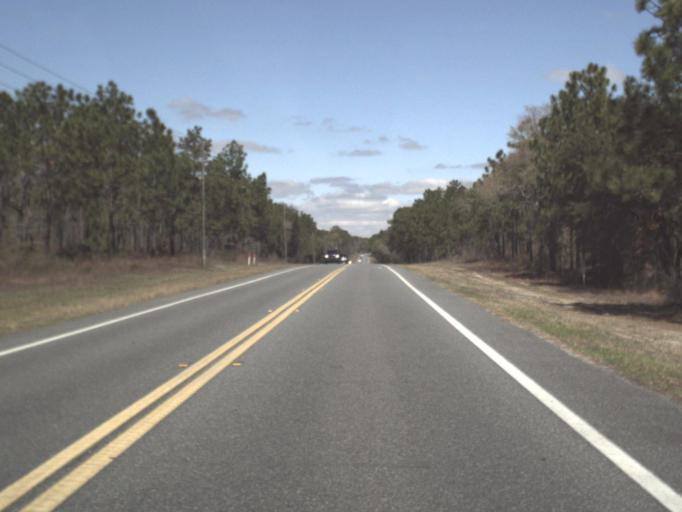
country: US
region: Florida
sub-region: Wakulla County
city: Crawfordville
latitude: 30.0667
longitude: -84.3888
